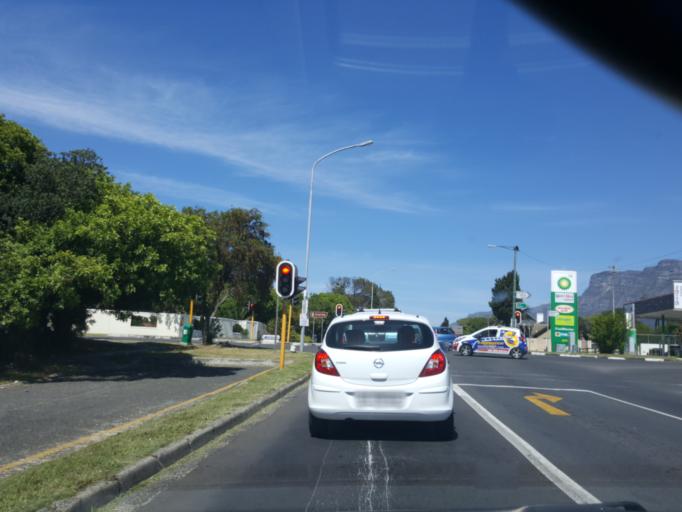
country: ZA
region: Western Cape
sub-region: City of Cape Town
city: Rosebank
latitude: -33.9407
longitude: 18.5009
